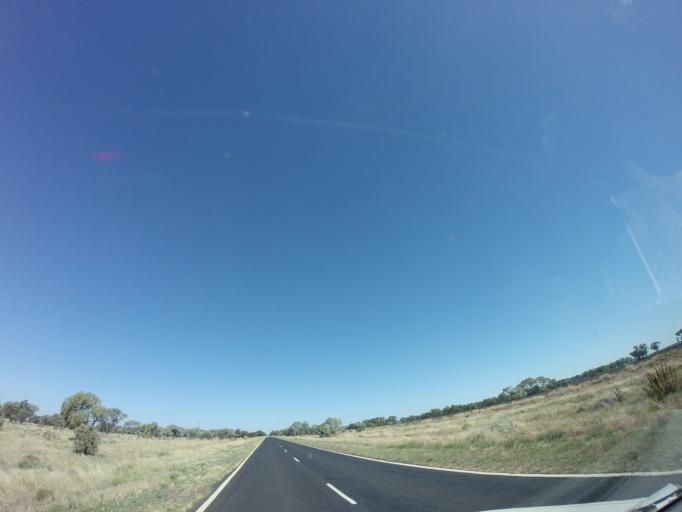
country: AU
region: New South Wales
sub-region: Bogan
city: Nyngan
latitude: -31.7780
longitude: 147.6044
